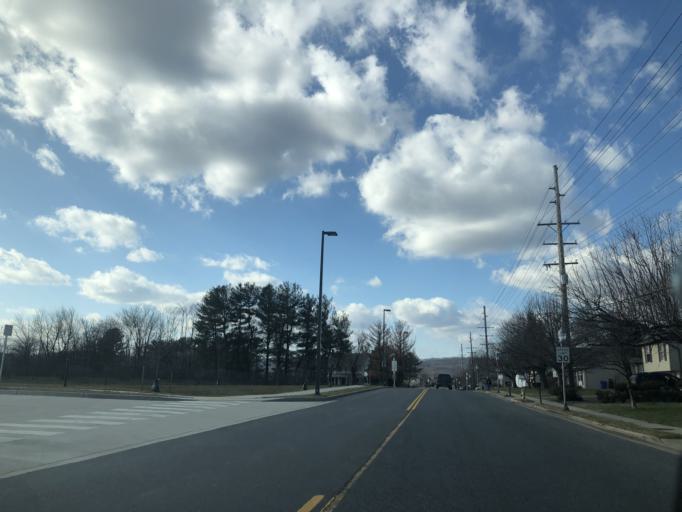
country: US
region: Maryland
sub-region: Frederick County
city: Ballenger Creek
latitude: 39.4098
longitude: -77.4562
